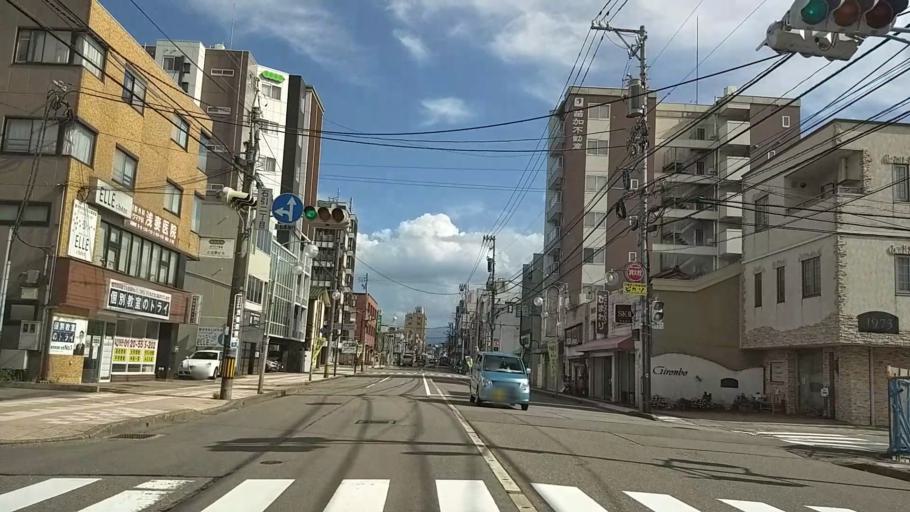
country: JP
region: Ishikawa
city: Nonoichi
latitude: 36.5559
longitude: 136.6699
